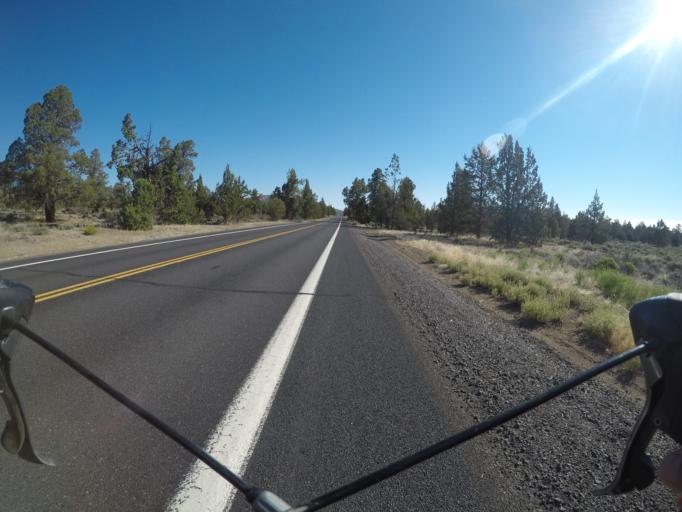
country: US
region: Oregon
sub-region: Deschutes County
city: Redmond
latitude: 44.2183
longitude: -121.3134
